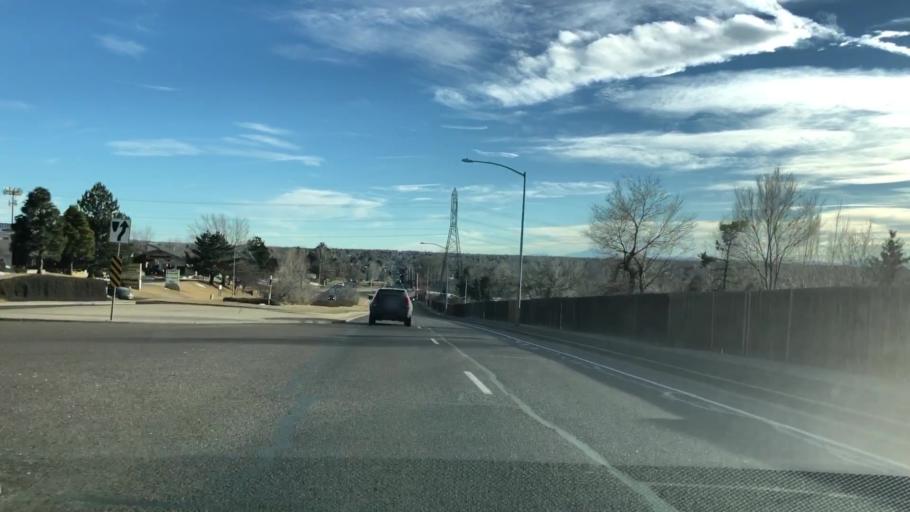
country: US
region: Colorado
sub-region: Adams County
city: Aurora
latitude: 39.6850
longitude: -104.7912
